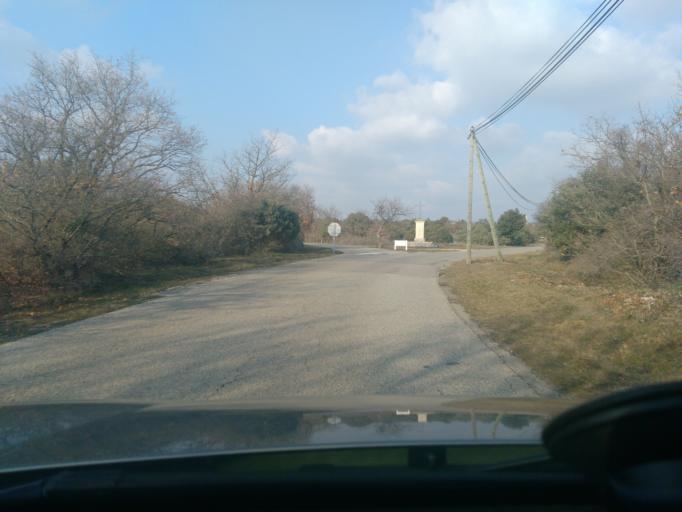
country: FR
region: Rhone-Alpes
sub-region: Departement de la Drome
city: Allan
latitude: 44.4687
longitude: 4.8420
